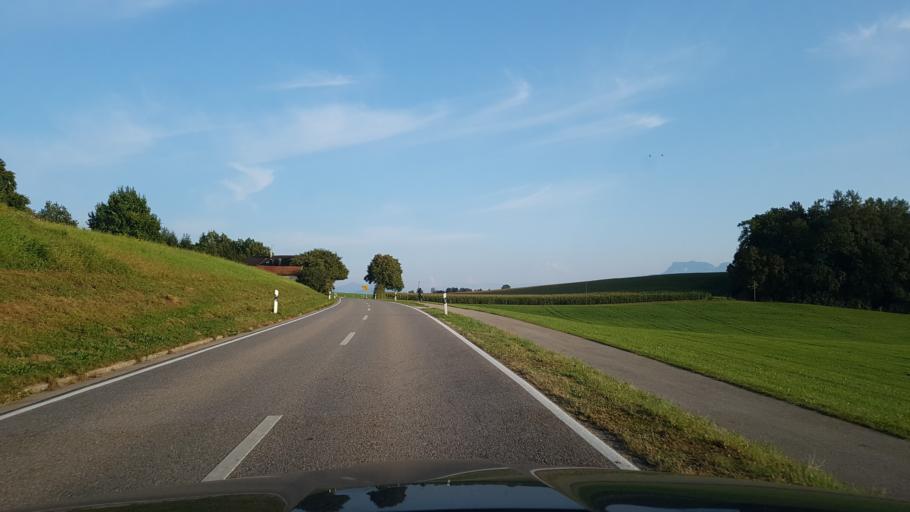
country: DE
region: Bavaria
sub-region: Upper Bavaria
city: Laufen
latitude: 47.8999
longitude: 12.9154
